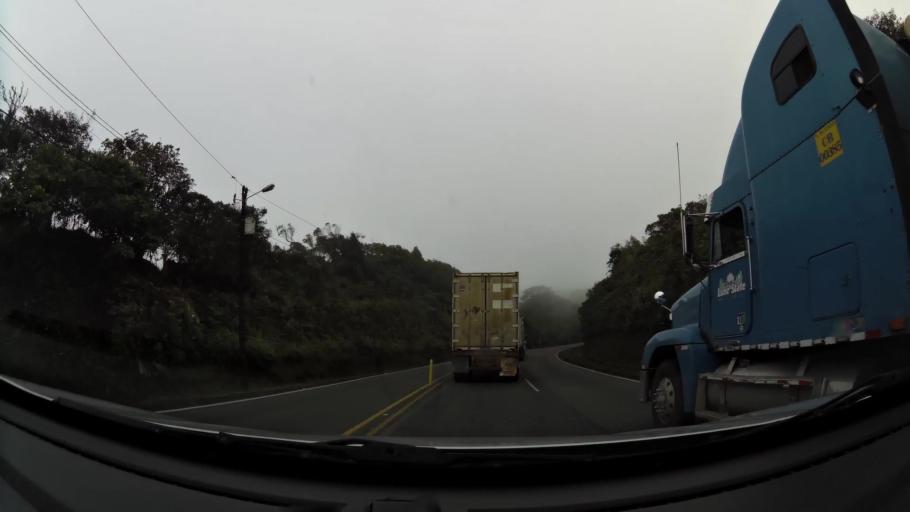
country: CR
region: Heredia
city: Angeles
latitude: 10.0477
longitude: -84.0074
